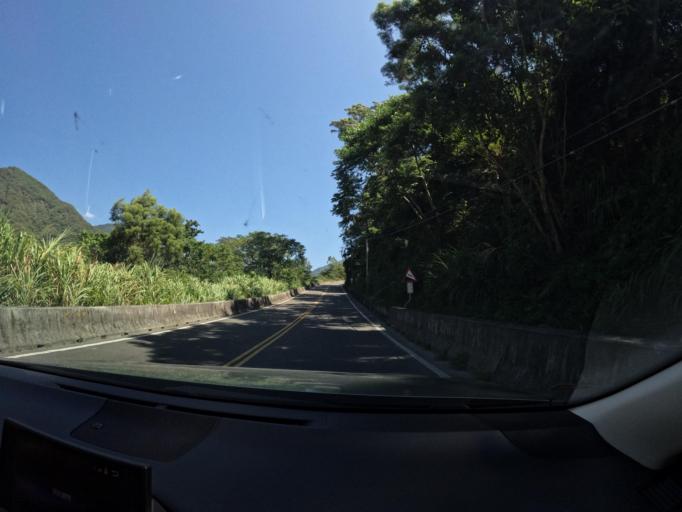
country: TW
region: Taiwan
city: Yujing
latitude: 23.1955
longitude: 120.7926
